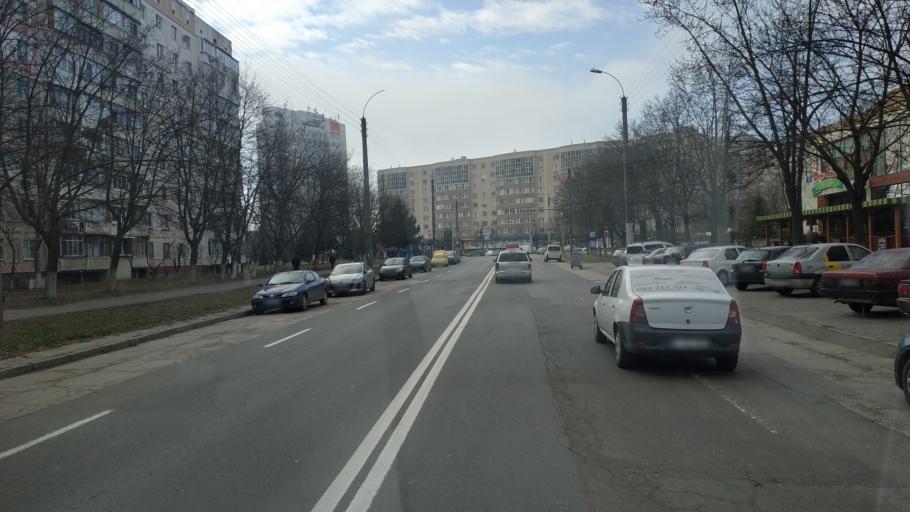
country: MD
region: Chisinau
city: Vatra
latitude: 47.0400
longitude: 28.7698
